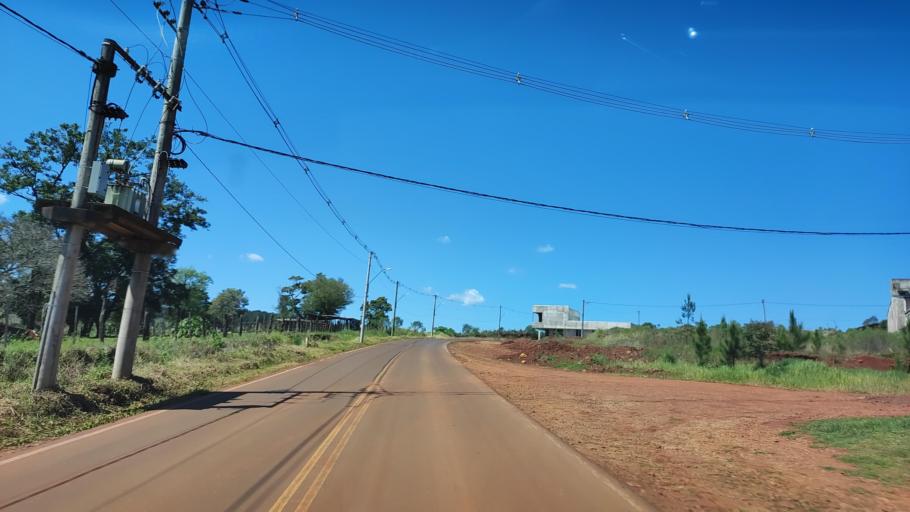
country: AR
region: Misiones
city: Puerto Rico
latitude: -26.8098
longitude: -55.0086
